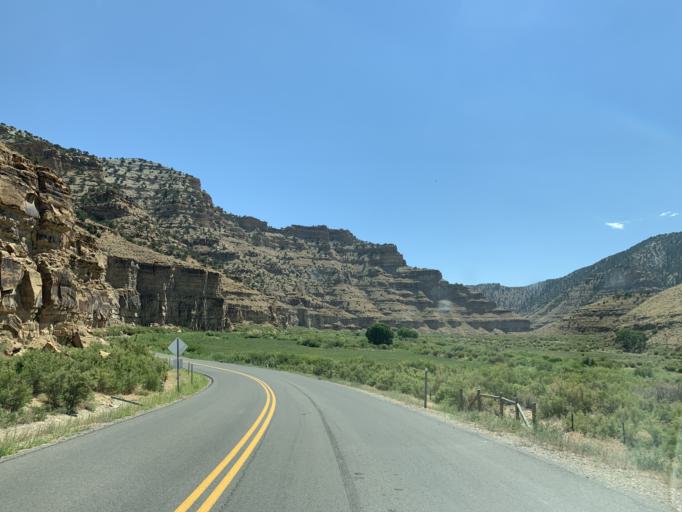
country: US
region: Utah
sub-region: Carbon County
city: East Carbon City
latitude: 39.8129
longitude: -110.2837
